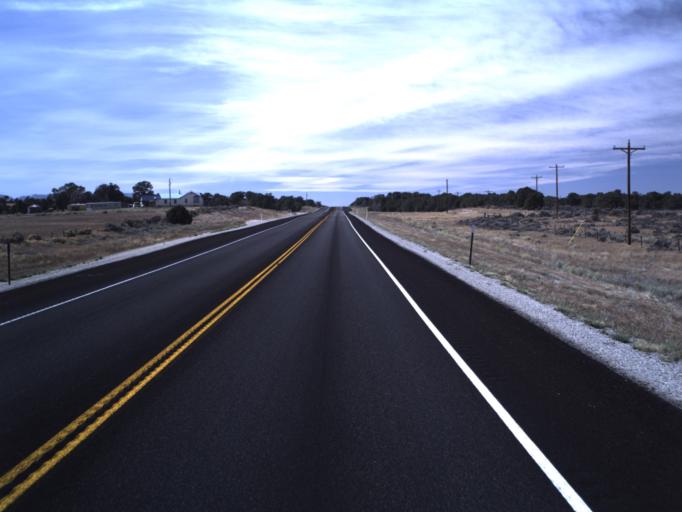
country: US
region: Colorado
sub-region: Dolores County
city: Dove Creek
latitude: 37.8208
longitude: -109.0568
